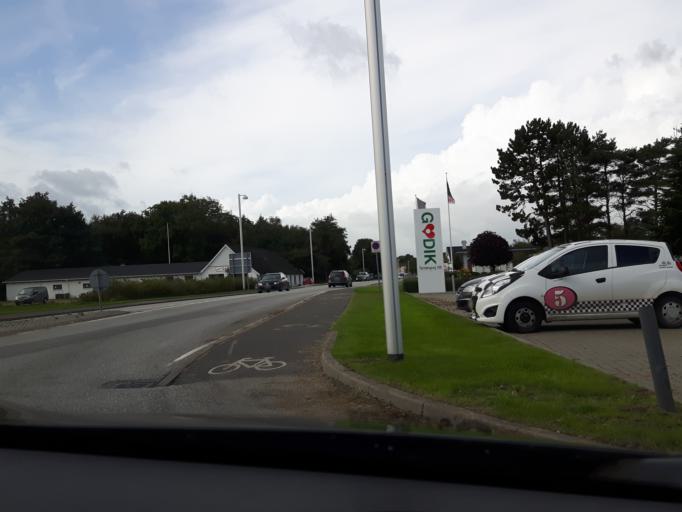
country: DK
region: North Denmark
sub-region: Jammerbugt Kommune
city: Brovst
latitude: 57.0988
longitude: 9.5367
